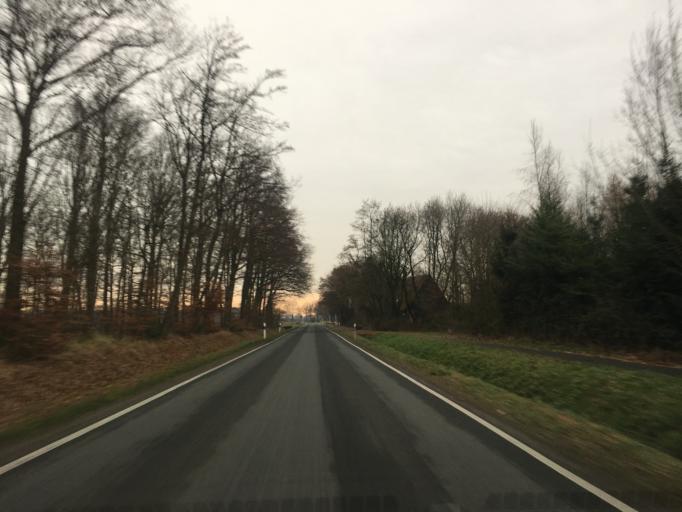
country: DE
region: North Rhine-Westphalia
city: Ludinghausen
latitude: 51.7311
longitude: 7.4476
